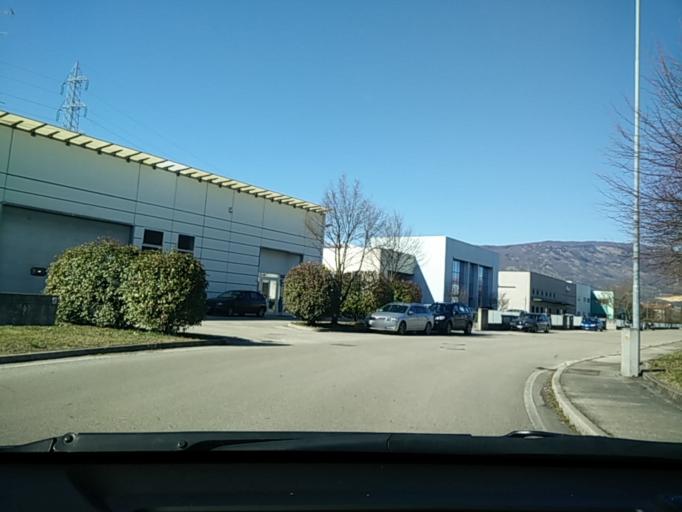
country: IT
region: Friuli Venezia Giulia
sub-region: Provincia di Pordenone
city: Caneva
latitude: 45.9436
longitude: 12.4580
